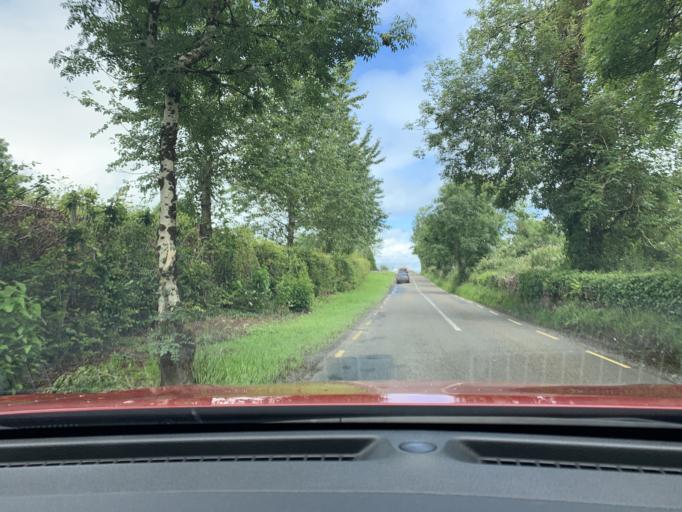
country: IE
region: Connaught
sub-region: County Leitrim
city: Carrick-on-Shannon
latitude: 53.9207
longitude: -8.1209
